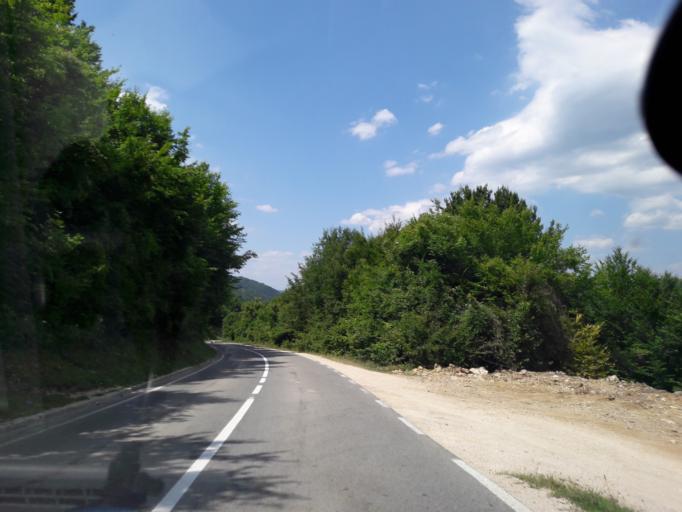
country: BA
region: Republika Srpska
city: Sipovo
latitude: 44.1988
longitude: 17.1515
